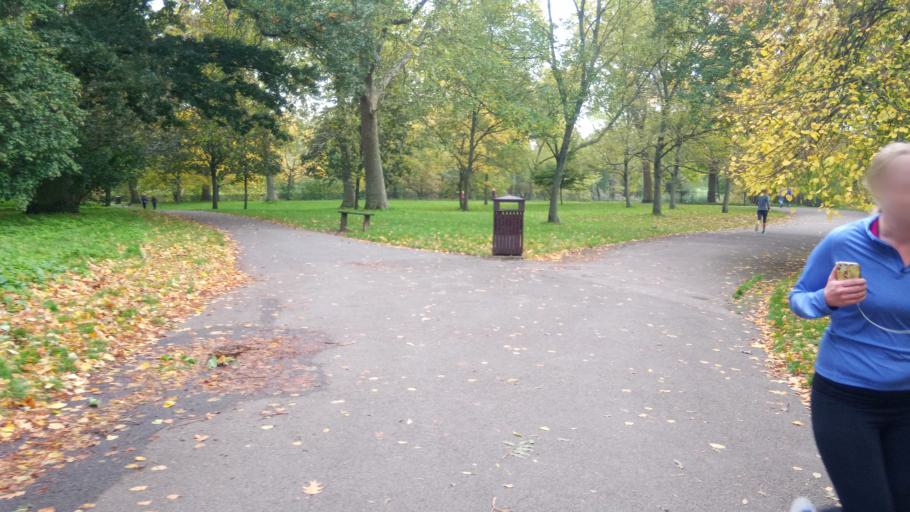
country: GB
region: England
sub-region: Greater London
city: Camden Town
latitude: 51.5292
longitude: -0.1601
